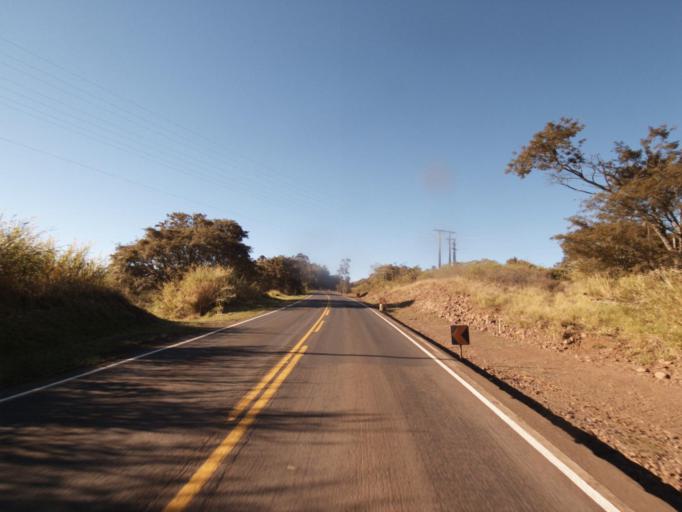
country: AR
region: Misiones
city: Bernardo de Irigoyen
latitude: -26.5013
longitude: -53.5077
